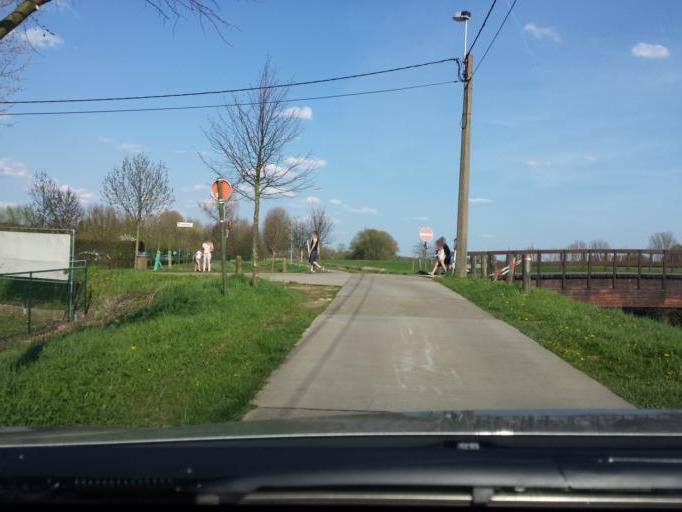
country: BE
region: Flanders
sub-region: Provincie Limburg
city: Herk-de-Stad
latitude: 50.9635
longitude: 5.1459
